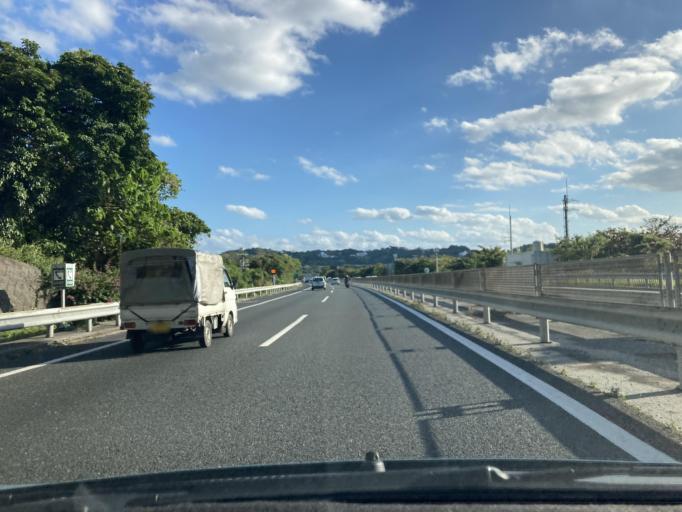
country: JP
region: Okinawa
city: Chatan
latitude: 26.3058
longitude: 127.7879
